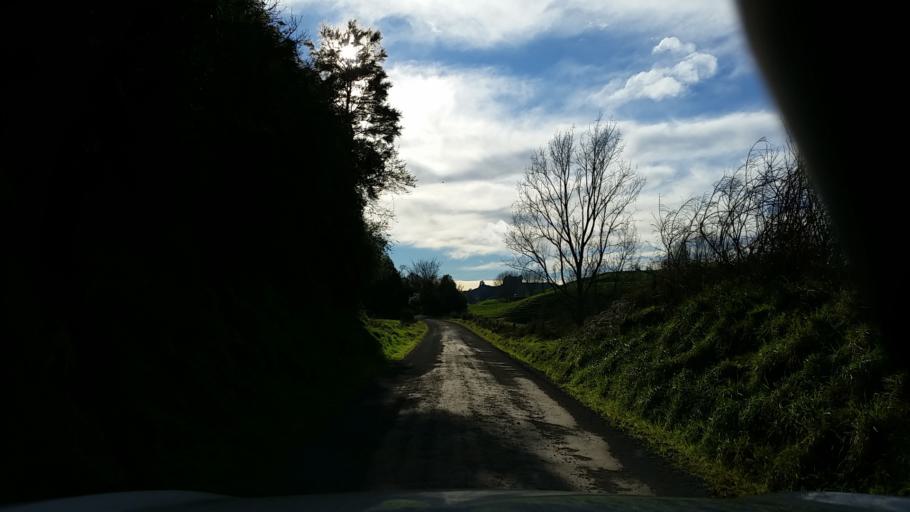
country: NZ
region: Waikato
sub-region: South Waikato District
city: Tokoroa
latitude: -38.3911
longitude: 176.0764
